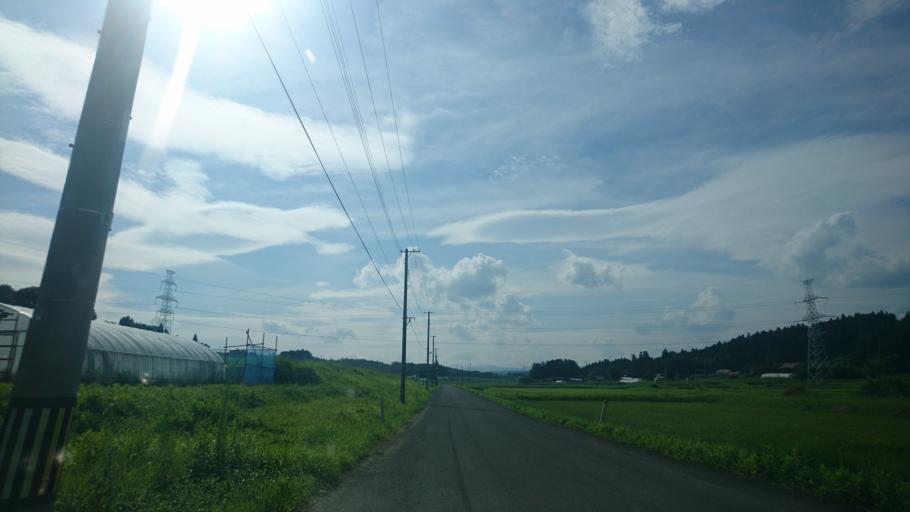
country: JP
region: Miyagi
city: Furukawa
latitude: 38.7619
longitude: 140.9794
